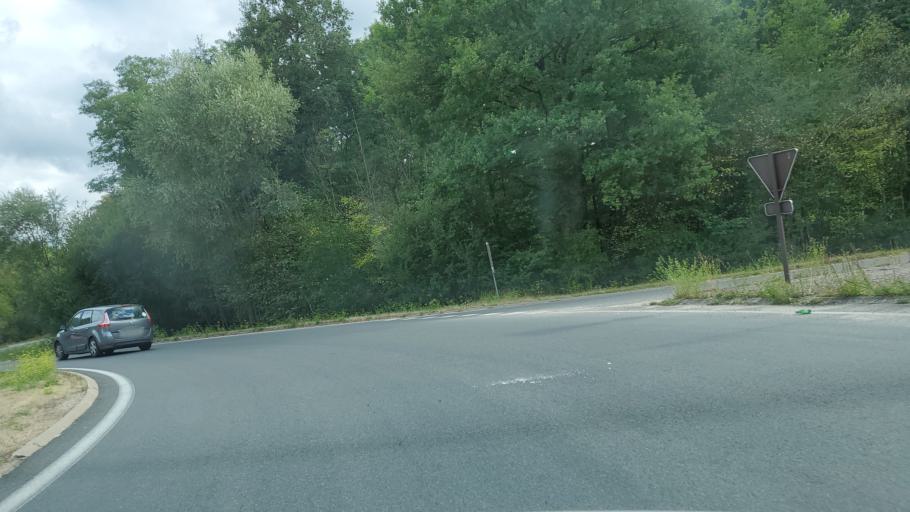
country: FR
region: Ile-de-France
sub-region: Departement de Seine-et-Marne
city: Villeneuve-le-Comte
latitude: 48.8151
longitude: 2.8415
